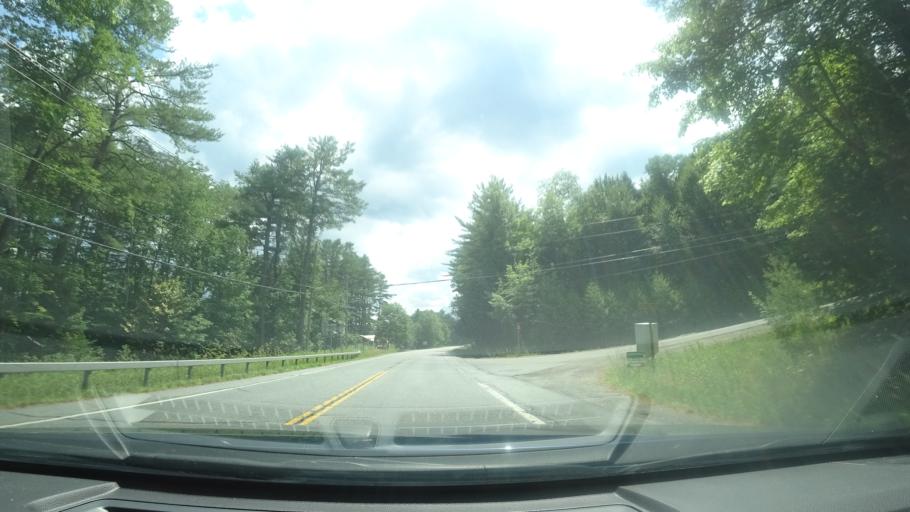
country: US
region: New York
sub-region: Warren County
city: Warrensburg
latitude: 43.5283
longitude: -73.7909
